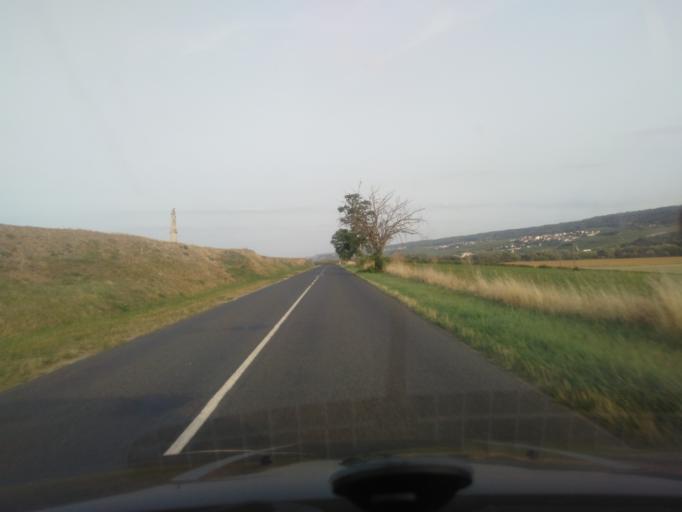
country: FR
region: Champagne-Ardenne
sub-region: Departement de la Marne
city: Mareuil-le-Port
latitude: 49.0898
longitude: 3.7691
